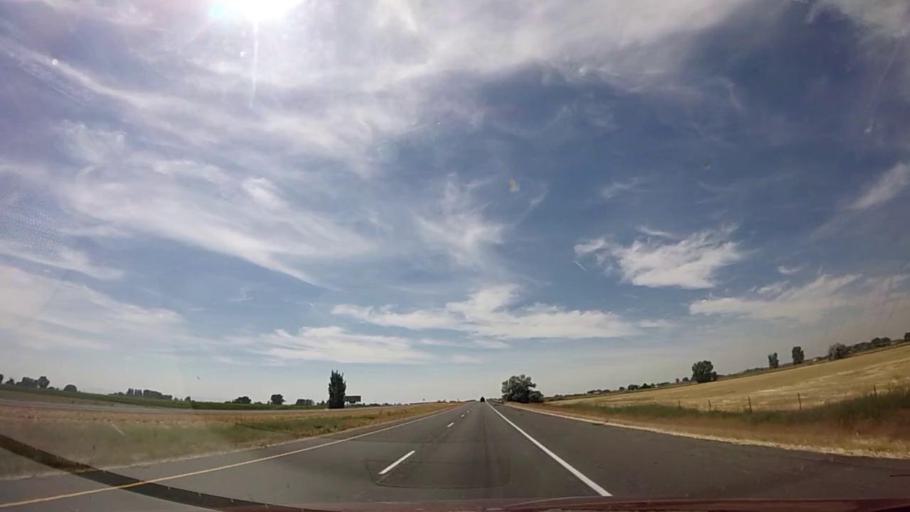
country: US
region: Idaho
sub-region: Minidoka County
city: Rupert
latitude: 42.5690
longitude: -113.6570
